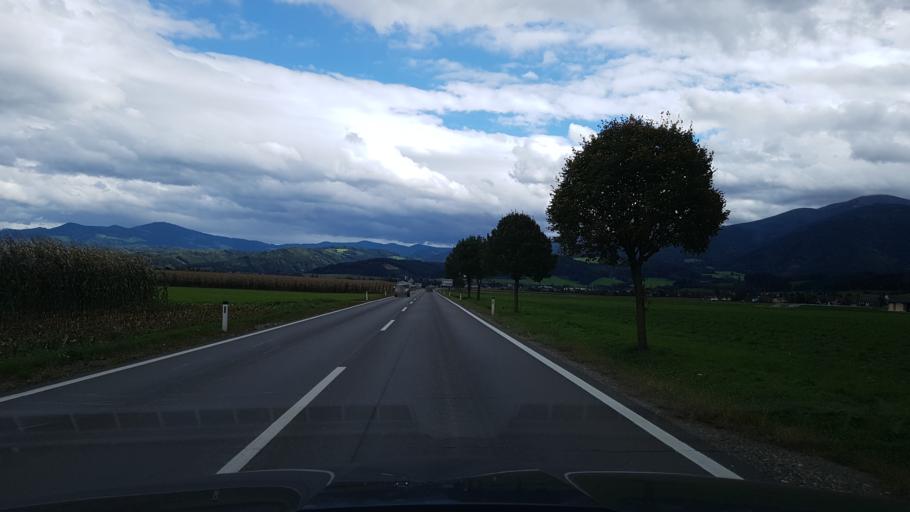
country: AT
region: Styria
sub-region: Politischer Bezirk Murtal
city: Weisskirchen in Steiermark
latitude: 47.1624
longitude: 14.7026
